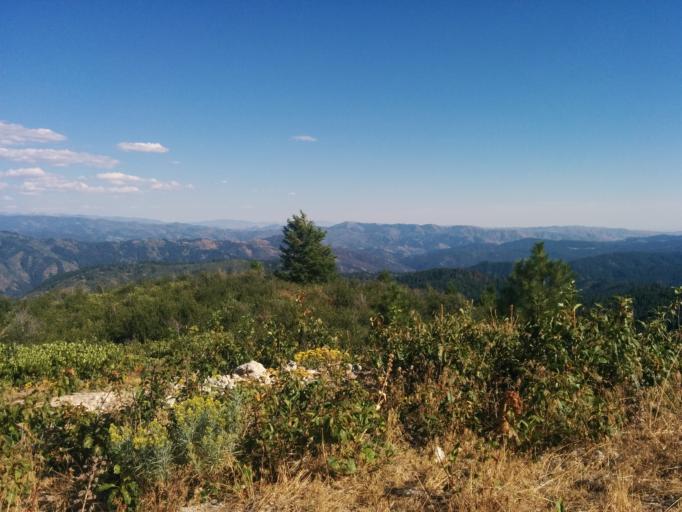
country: US
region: Idaho
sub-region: Boise County
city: Idaho City
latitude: 43.8370
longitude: -116.0333
